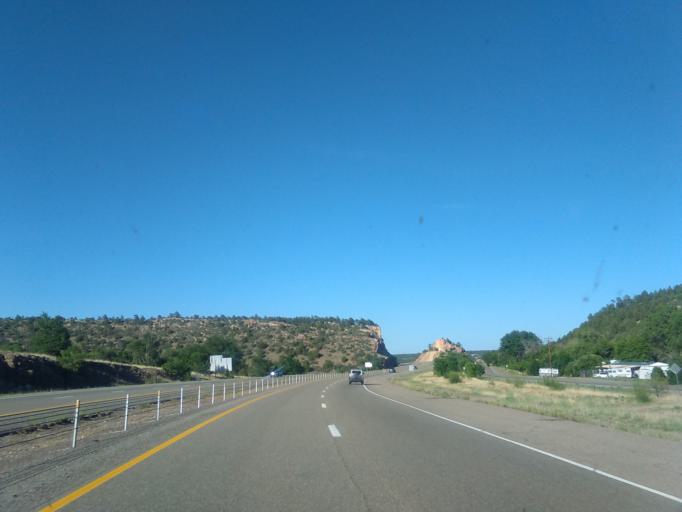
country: US
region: New Mexico
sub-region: San Miguel County
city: Las Vegas
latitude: 35.5238
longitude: -105.2460
